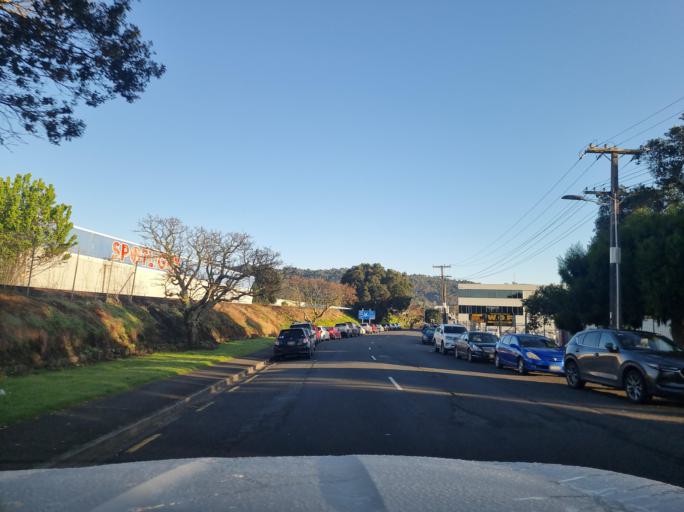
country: NZ
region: Northland
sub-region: Whangarei
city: Whangarei
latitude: -35.7291
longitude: 174.3207
